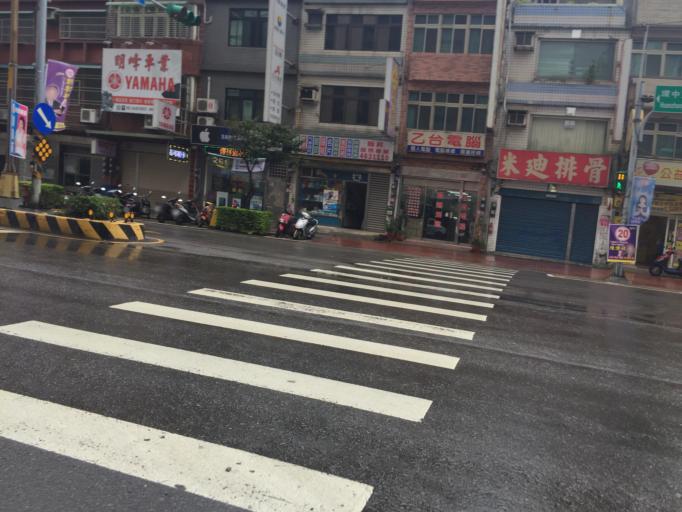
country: TW
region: Taiwan
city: Taoyuan City
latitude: 24.9660
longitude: 121.2592
